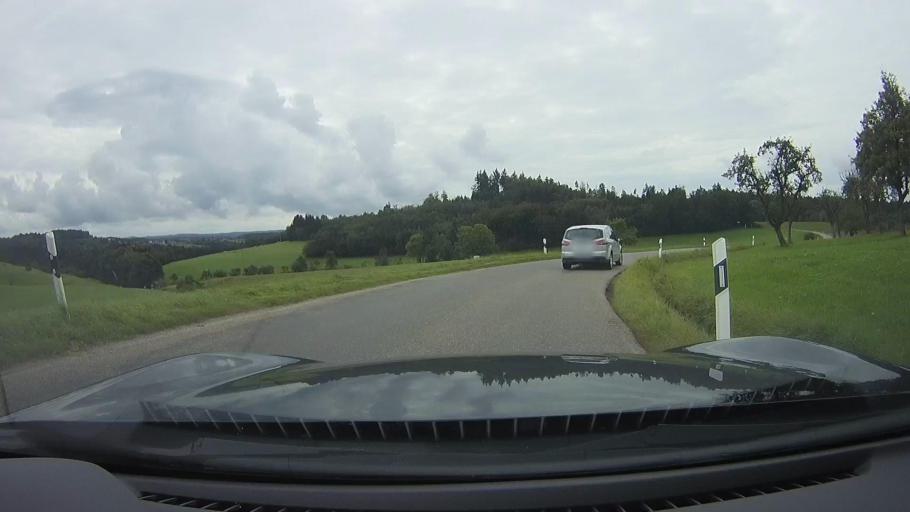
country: DE
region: Baden-Wuerttemberg
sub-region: Regierungsbezirk Stuttgart
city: Murrhardt
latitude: 49.0238
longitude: 9.5641
